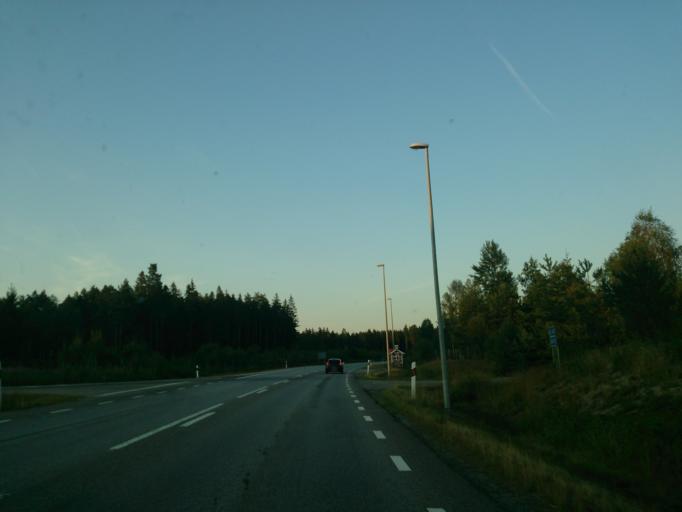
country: SE
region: Kronoberg
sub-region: Alvesta Kommun
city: Alvesta
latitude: 56.9131
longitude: 14.4827
